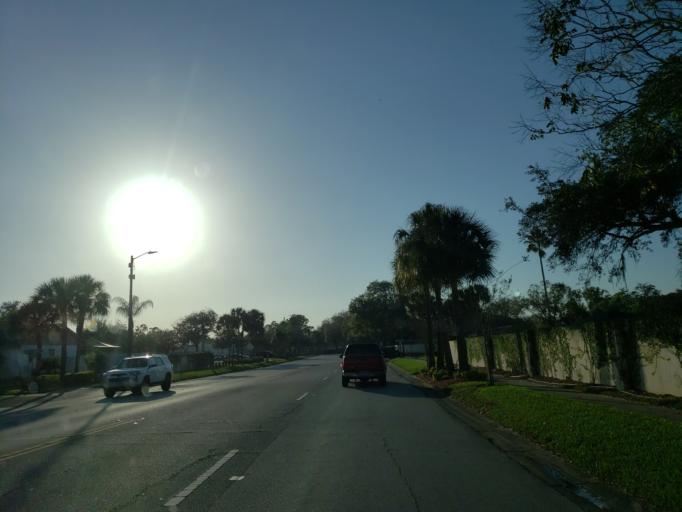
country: US
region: Florida
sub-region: Hillsborough County
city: Bloomingdale
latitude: 27.8847
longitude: -82.2623
